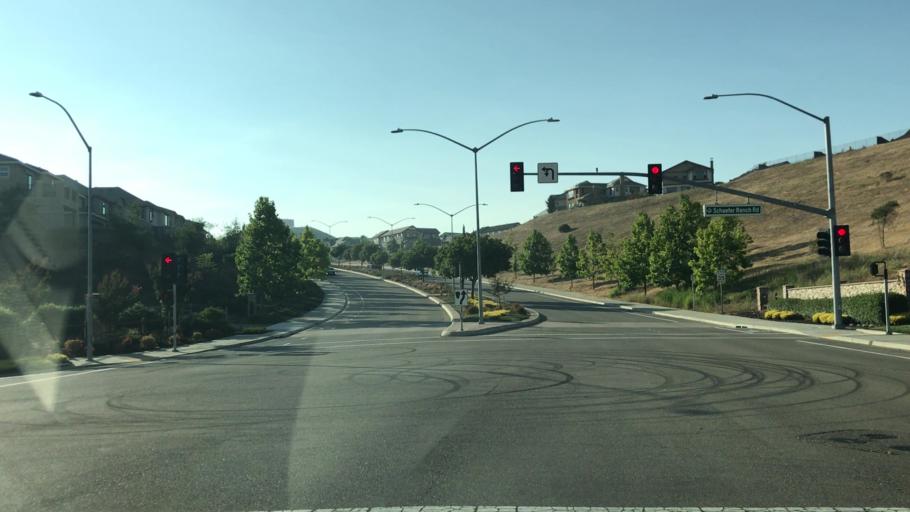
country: US
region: California
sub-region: Alameda County
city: Dublin
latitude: 37.7021
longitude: -121.9768
